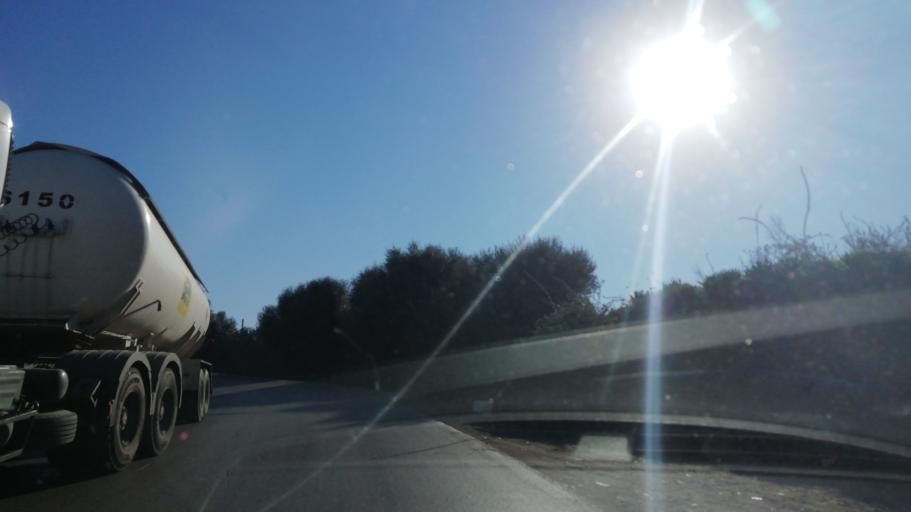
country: DZ
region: Relizane
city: Smala
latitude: 35.7034
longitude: 0.7697
